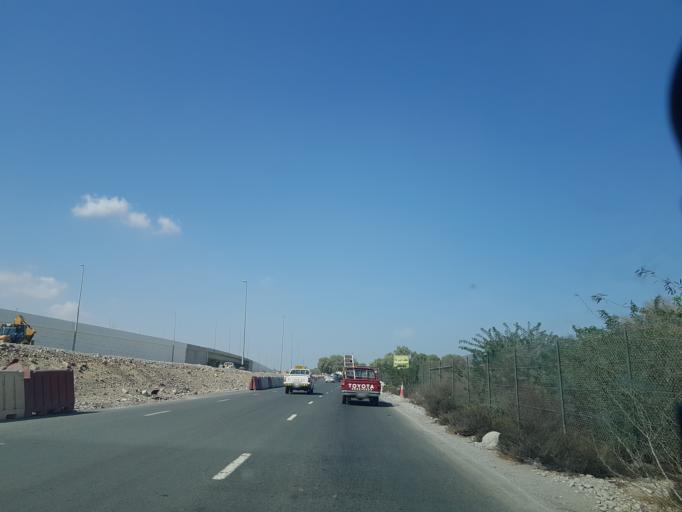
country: AE
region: Ra's al Khaymah
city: Ras al-Khaimah
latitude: 25.6997
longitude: 55.9705
